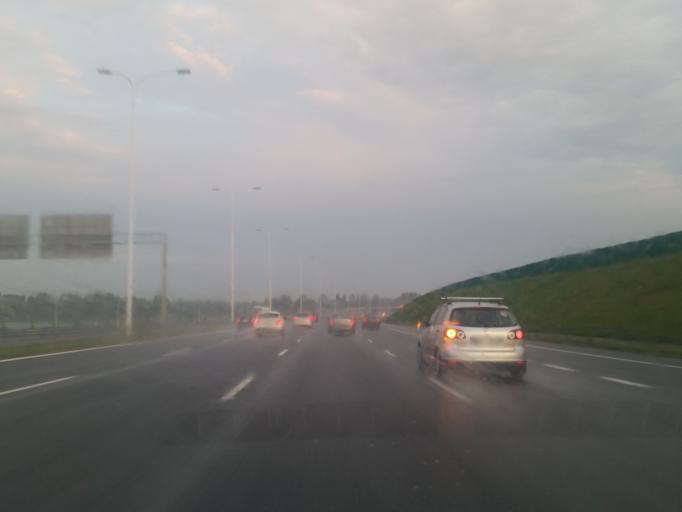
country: PL
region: Masovian Voivodeship
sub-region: Powiat pruszkowski
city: Rybie
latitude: 52.1604
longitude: 20.9503
